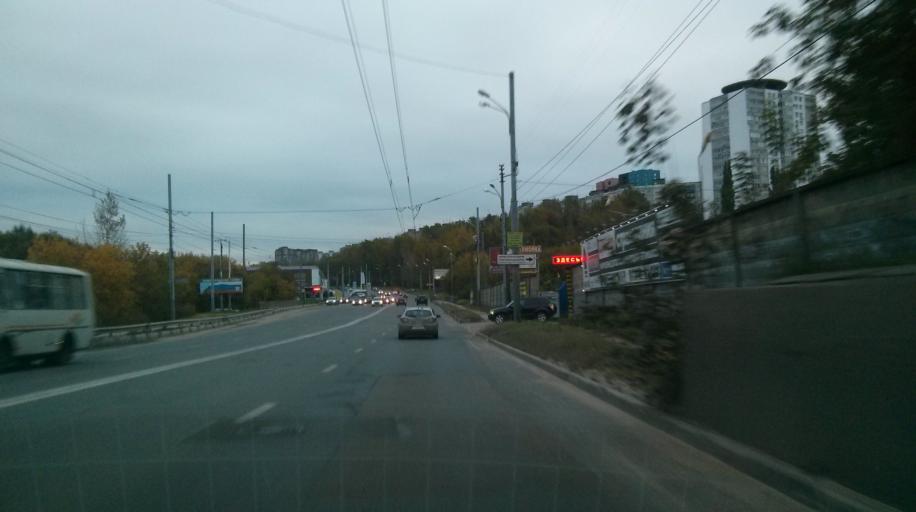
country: RU
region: Nizjnij Novgorod
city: Afonino
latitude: 56.3017
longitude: 44.0534
